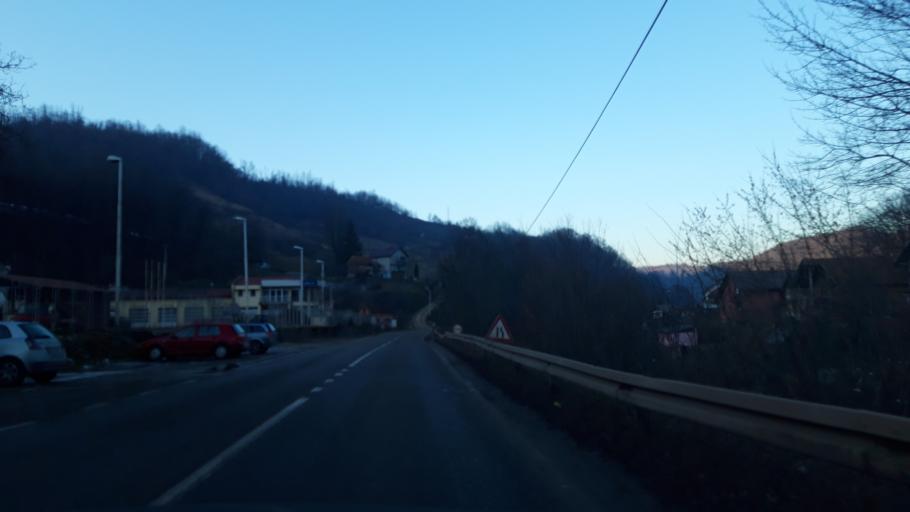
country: BA
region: Republika Srpska
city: Milici
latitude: 44.1761
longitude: 19.0743
